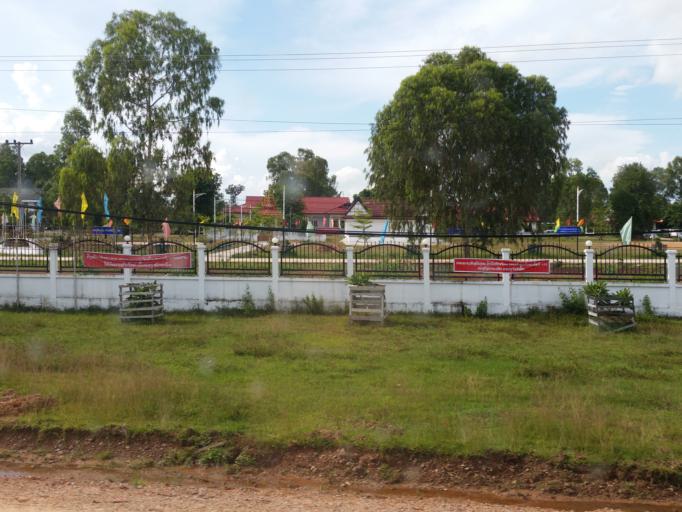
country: LA
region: Champasak
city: Pakxe
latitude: 15.1037
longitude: 105.7414
